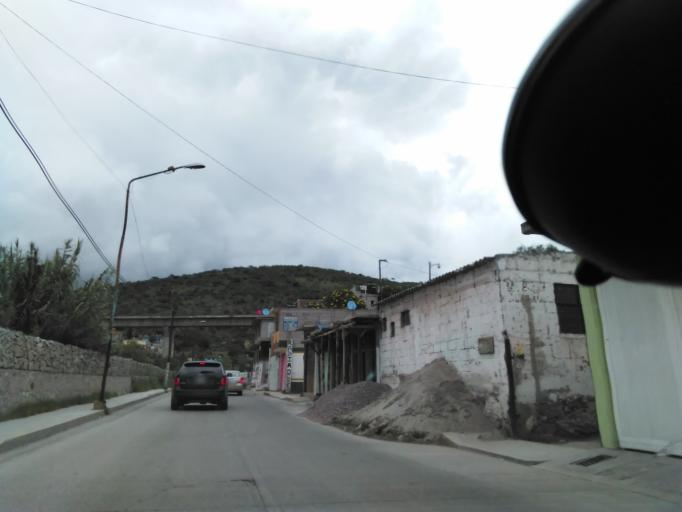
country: MX
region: Hidalgo
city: Tula de Allende
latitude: 20.0601
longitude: -99.3444
